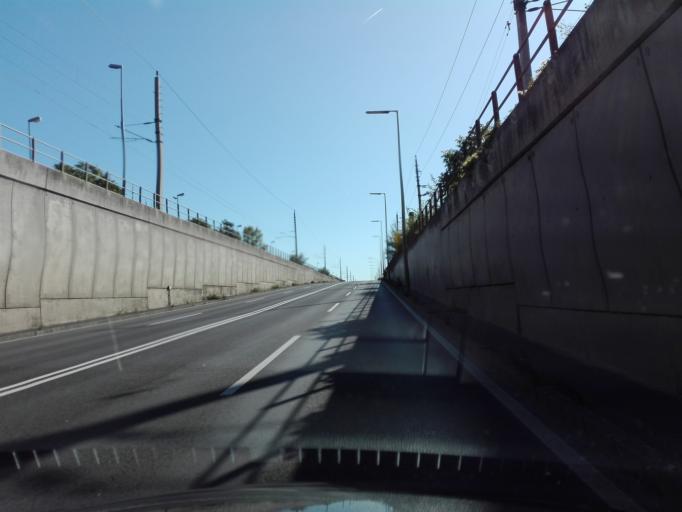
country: AT
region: Upper Austria
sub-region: Linz Stadt
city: Linz
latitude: 48.2720
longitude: 14.3200
